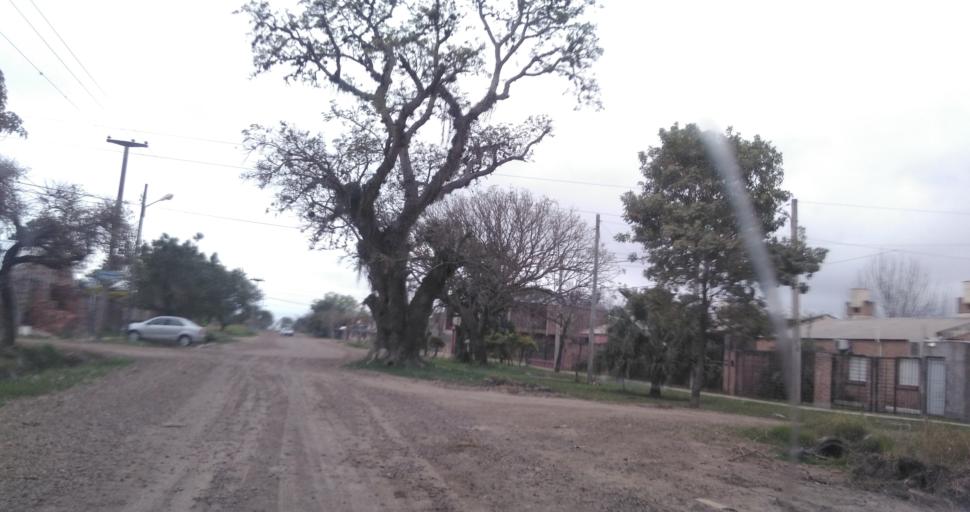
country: AR
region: Chaco
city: Fontana
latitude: -27.4455
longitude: -59.0358
